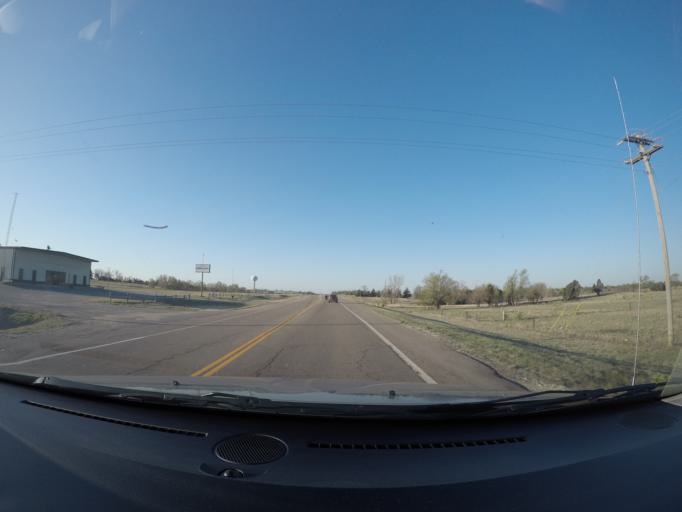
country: US
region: Kansas
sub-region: Pratt County
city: Pratt
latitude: 37.6648
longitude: -98.7164
